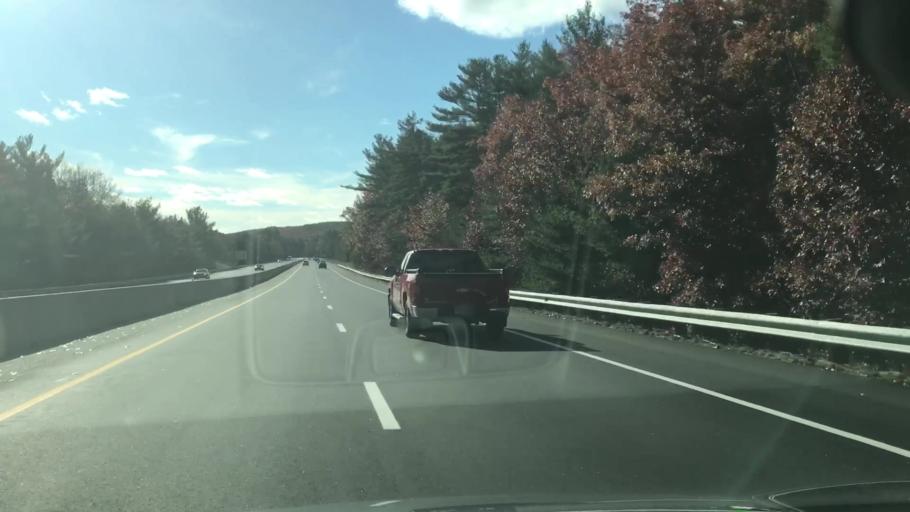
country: US
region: New Hampshire
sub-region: Merrimack County
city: South Hooksett
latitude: 43.0423
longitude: -71.4762
